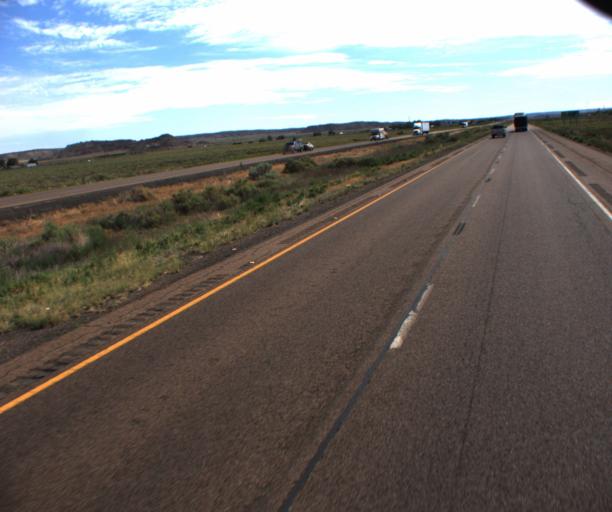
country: US
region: Arizona
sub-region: Apache County
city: Houck
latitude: 35.1936
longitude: -109.4203
